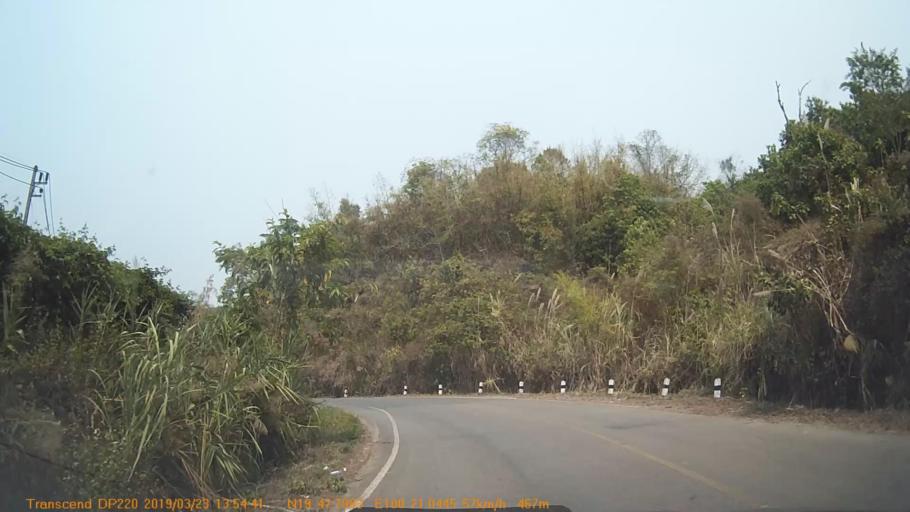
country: TH
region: Chiang Rai
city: Khun Tan
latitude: 19.7966
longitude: 100.3507
